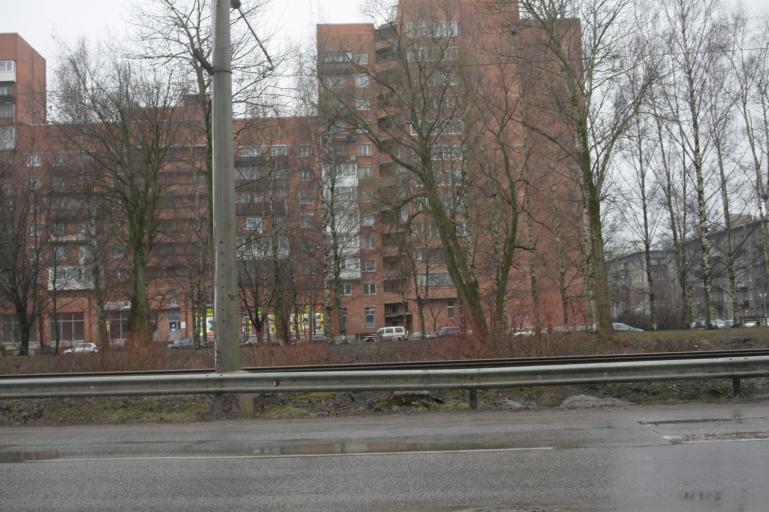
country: RU
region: St.-Petersburg
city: Komendantsky aerodrom
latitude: 59.9880
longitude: 30.2690
